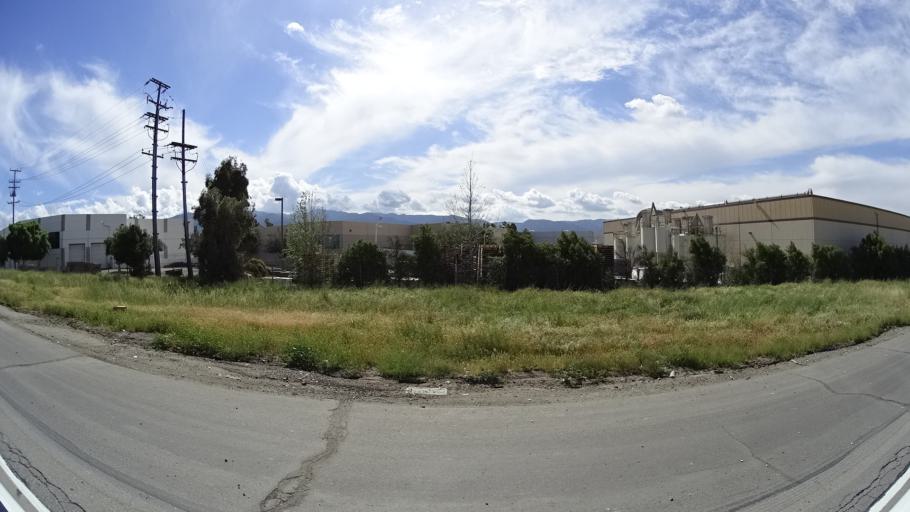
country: US
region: California
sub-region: Riverside County
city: Home Gardens
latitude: 33.8609
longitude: -117.5376
